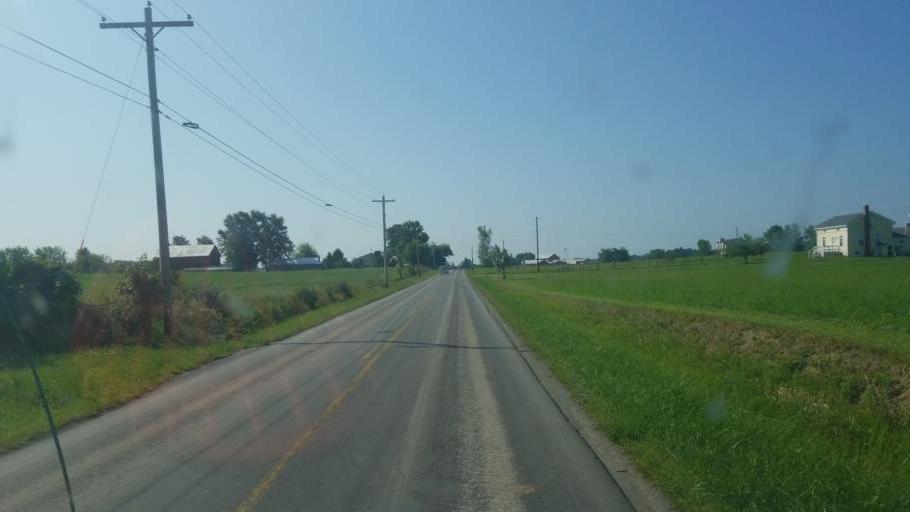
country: US
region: Ohio
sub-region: Wayne County
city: West Salem
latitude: 41.0105
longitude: -82.1640
